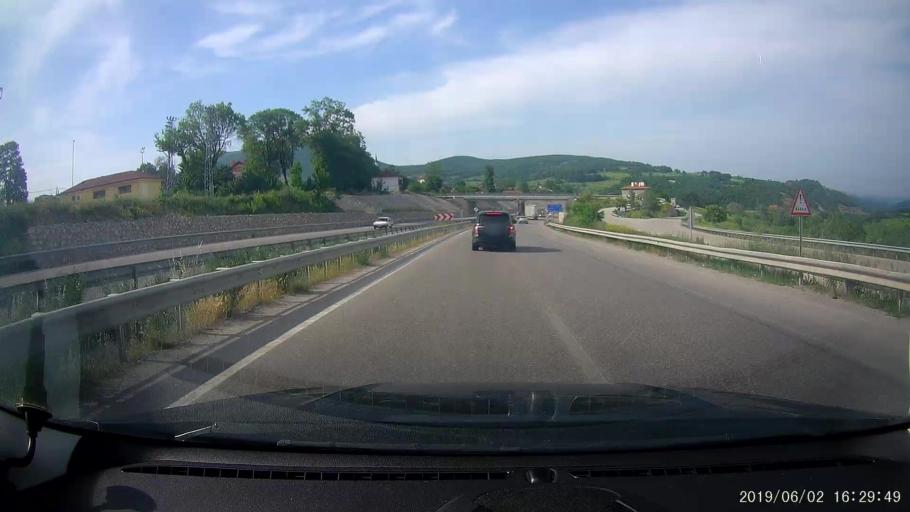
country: TR
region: Samsun
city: Ladik
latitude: 41.0180
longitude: 35.8724
